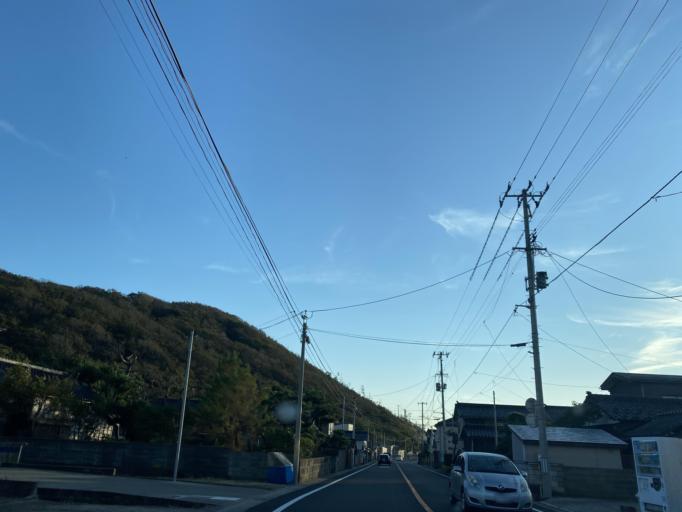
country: JP
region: Niigata
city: Kashiwazaki
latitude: 37.4568
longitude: 138.6103
